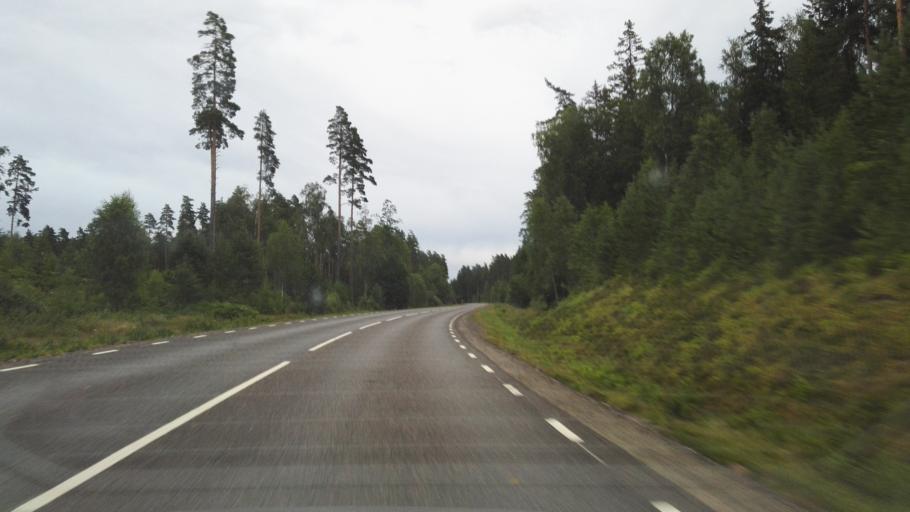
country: SE
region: Kronoberg
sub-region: Vaxjo Kommun
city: Braas
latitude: 57.0546
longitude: 15.0487
